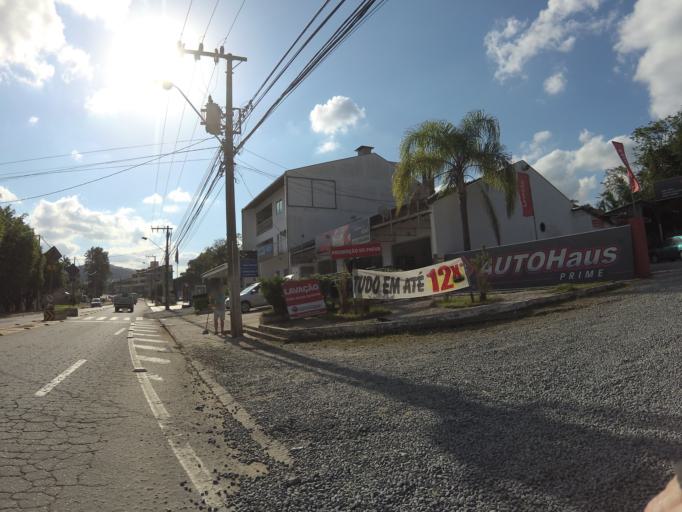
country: BR
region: Santa Catarina
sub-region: Blumenau
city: Blumenau
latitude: -26.8992
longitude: -49.1399
